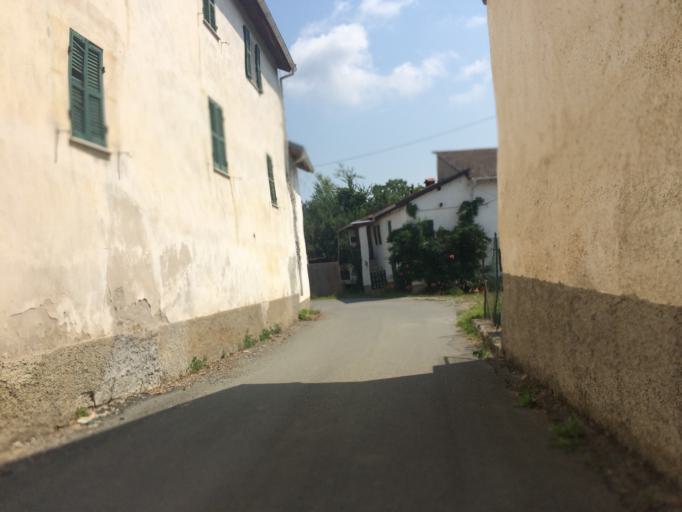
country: IT
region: Piedmont
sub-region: Provincia di Alessandria
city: Pareto
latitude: 44.4951
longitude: 8.3554
